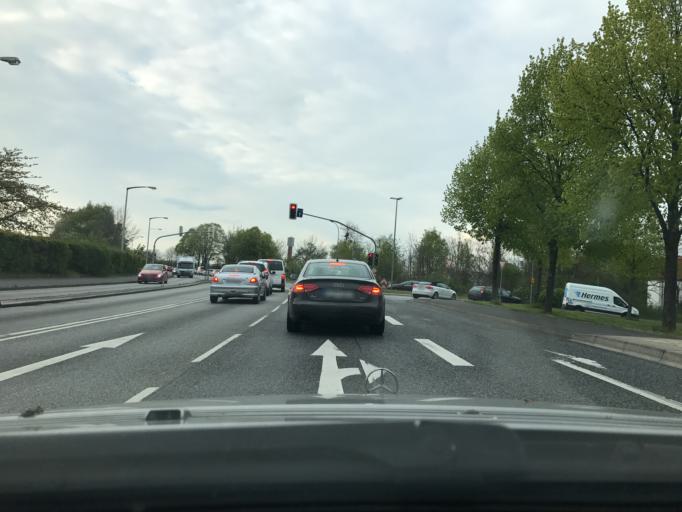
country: DE
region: Hesse
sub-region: Regierungsbezirk Kassel
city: Kassel
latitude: 51.3030
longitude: 9.5169
